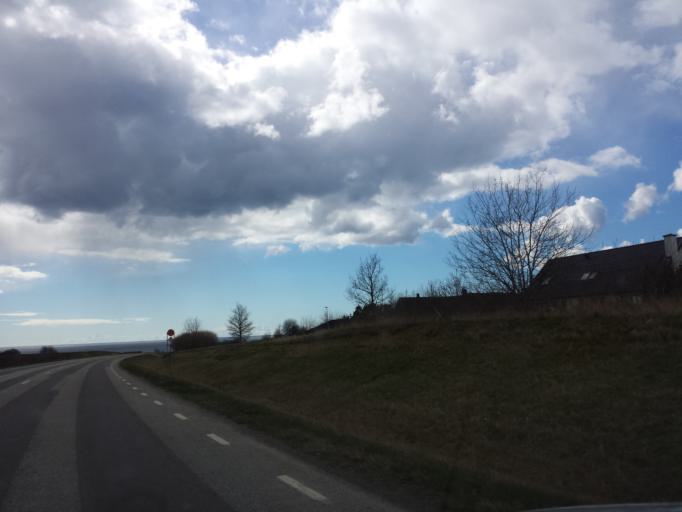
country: SE
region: Skane
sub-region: Ystads Kommun
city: Ystad
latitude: 55.4345
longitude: 13.7193
